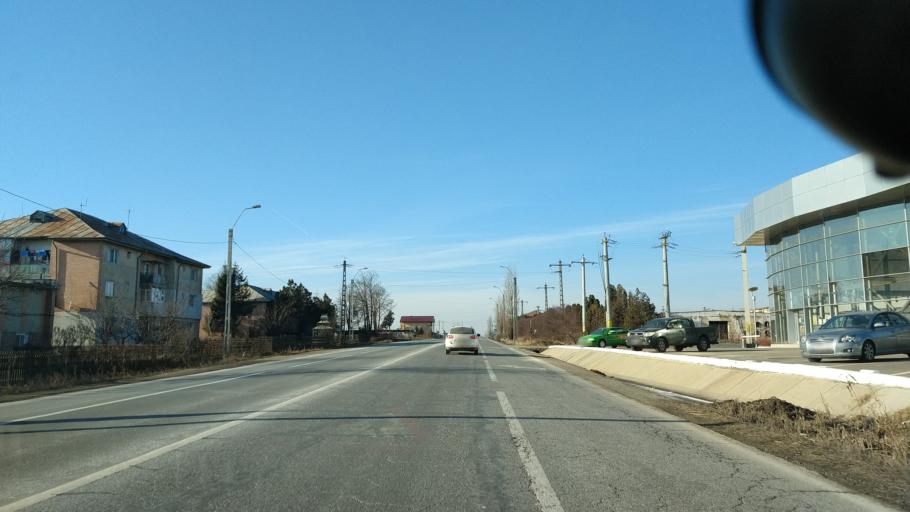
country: RO
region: Iasi
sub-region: Comuna Letcani
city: Letcani
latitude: 47.1852
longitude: 27.4527
